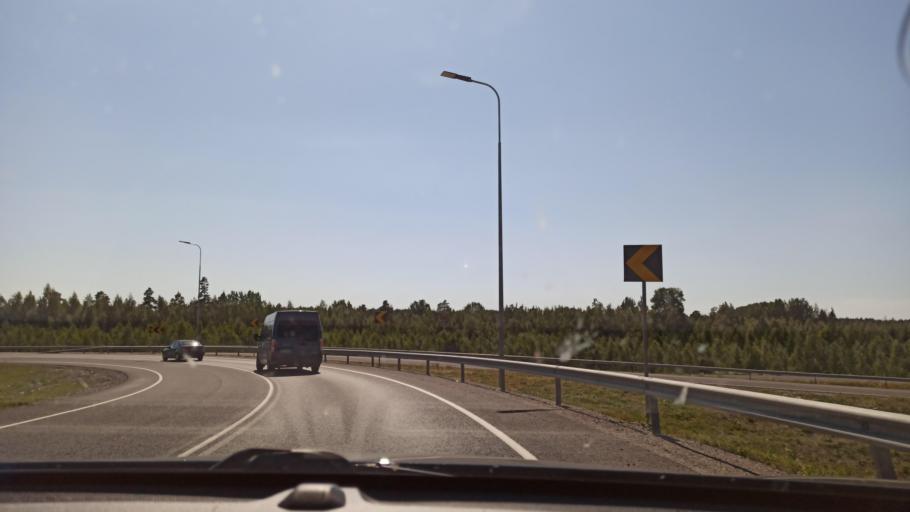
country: FI
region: Satakunta
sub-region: Pori
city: Noormarkku
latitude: 61.5615
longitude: 21.8091
